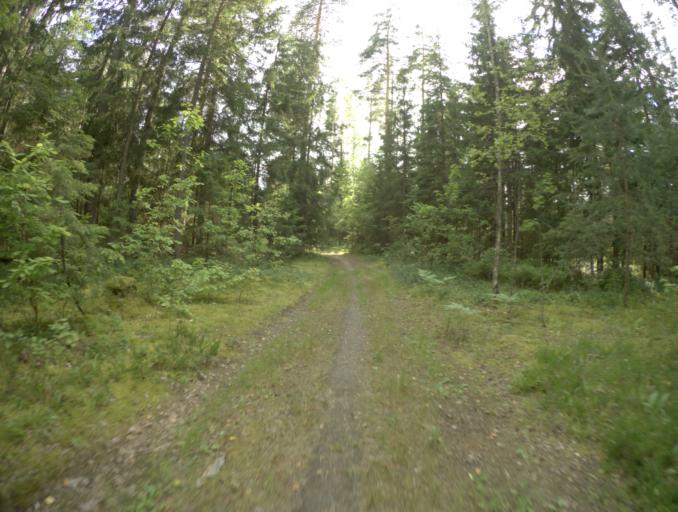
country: RU
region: Vladimir
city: Bogolyubovo
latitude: 56.0966
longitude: 40.5477
